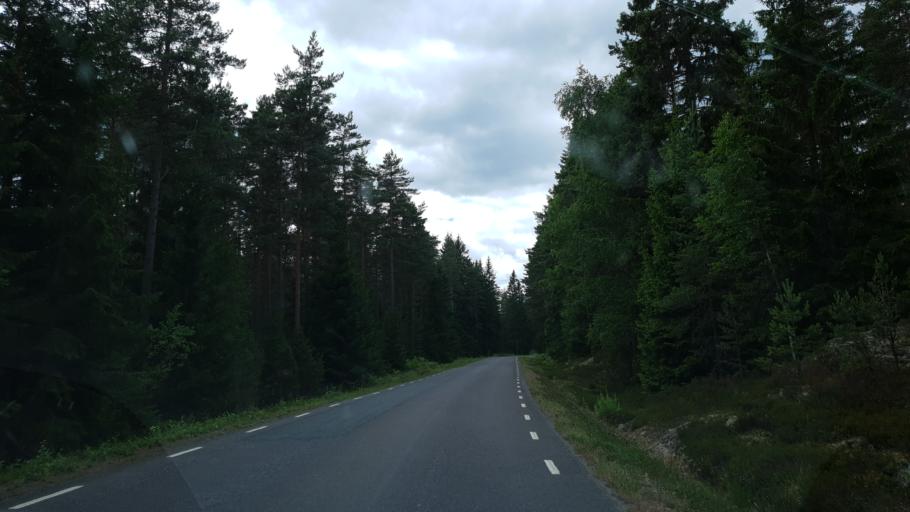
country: SE
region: Kalmar
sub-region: Hultsfreds Kommun
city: Virserum
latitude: 57.0679
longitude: 15.6048
